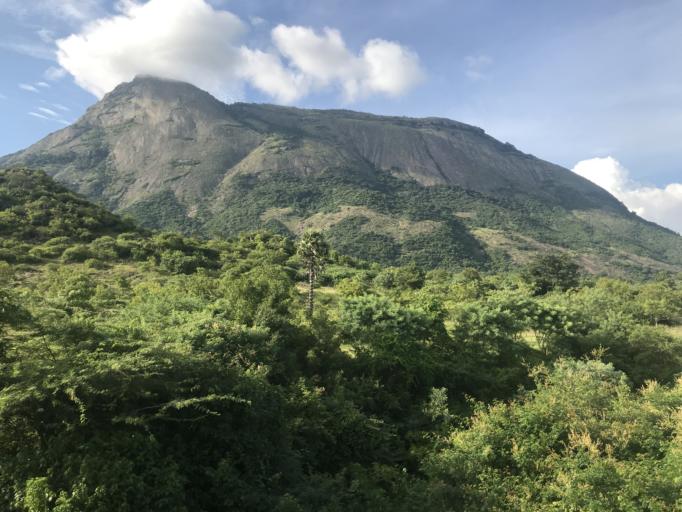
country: IN
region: Tamil Nadu
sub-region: Coimbatore
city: Madukkarai
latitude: 10.8971
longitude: 76.8903
